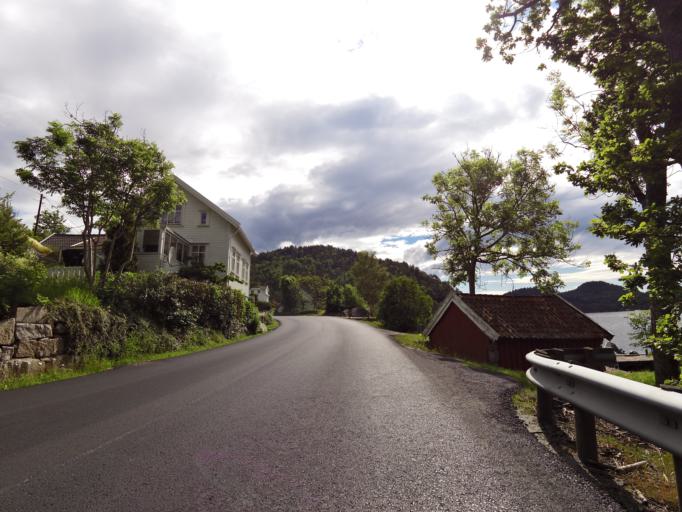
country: NO
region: Vest-Agder
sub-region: Lindesnes
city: Vigeland
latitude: 58.0512
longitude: 7.2455
